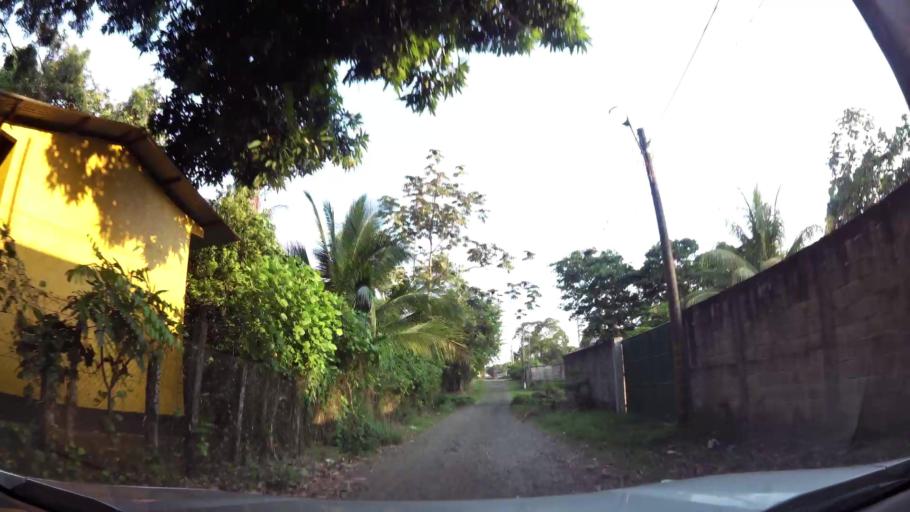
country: GT
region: Retalhuleu
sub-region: Municipio de Retalhuleu
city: Retalhuleu
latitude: 14.5468
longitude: -91.6649
